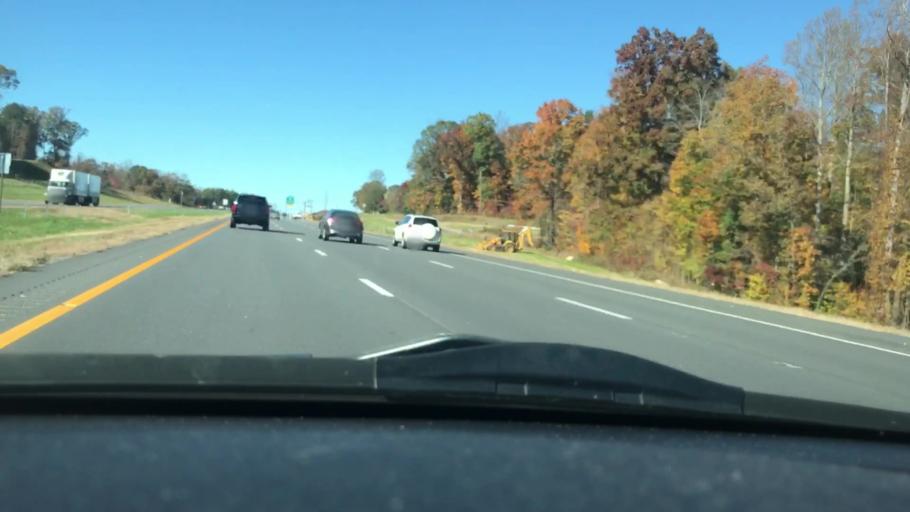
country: US
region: North Carolina
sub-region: Guilford County
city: Summerfield
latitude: 36.2321
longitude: -79.9157
